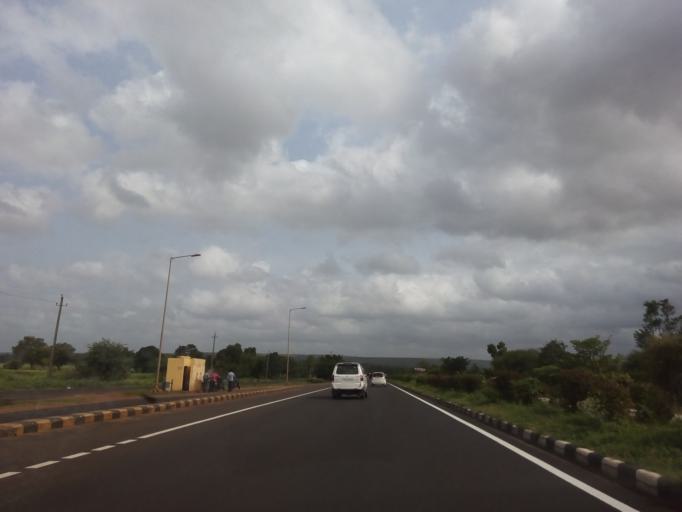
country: IN
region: Karnataka
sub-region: Belgaum
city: Hukeri
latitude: 16.1026
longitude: 74.5181
